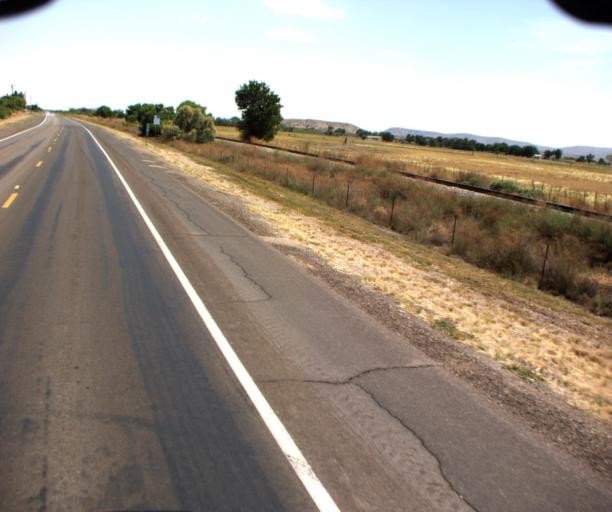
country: US
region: Arizona
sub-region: Greenlee County
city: Clifton
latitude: 32.6963
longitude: -109.0880
